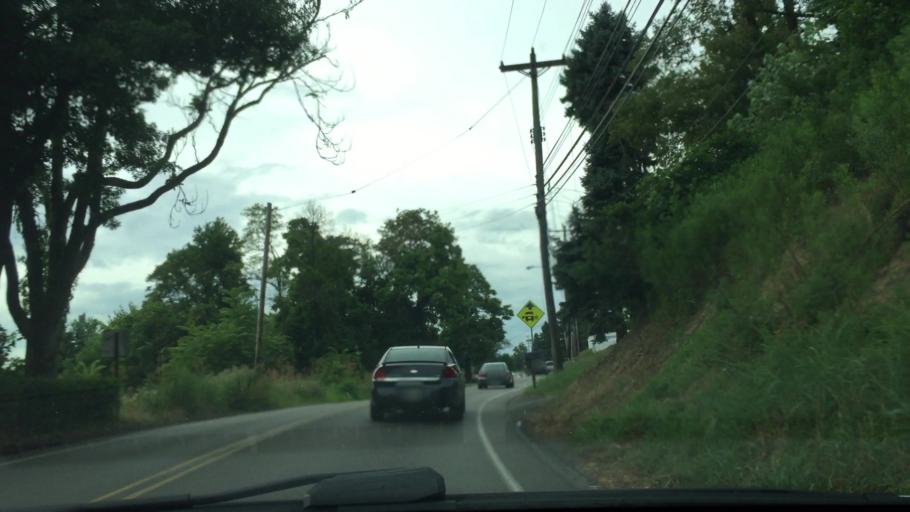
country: US
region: Pennsylvania
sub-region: Allegheny County
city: Ingram
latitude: 40.4524
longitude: -80.1092
